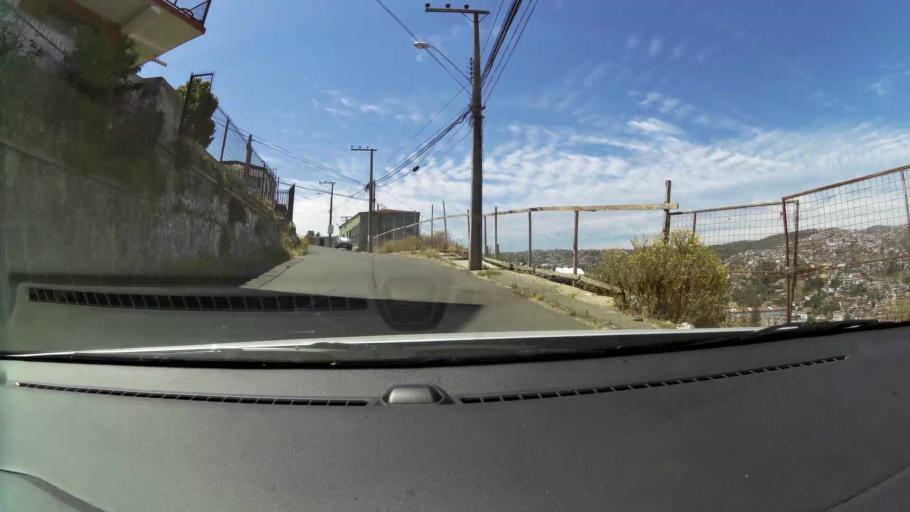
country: CL
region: Valparaiso
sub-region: Provincia de Valparaiso
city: Valparaiso
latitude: -33.0471
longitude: -71.6015
